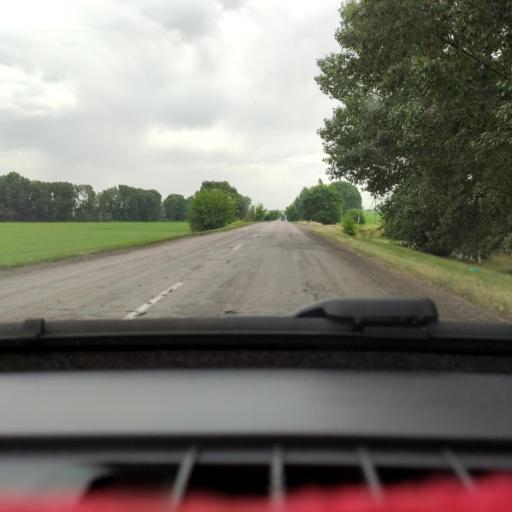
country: RU
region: Voronezj
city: Davydovka
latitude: 51.2465
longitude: 39.5751
